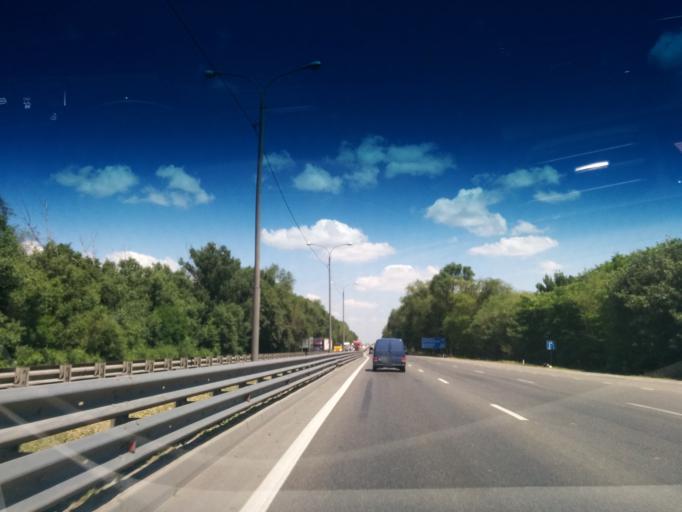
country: RU
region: Rostov
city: Aksay
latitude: 47.2931
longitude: 39.8552
